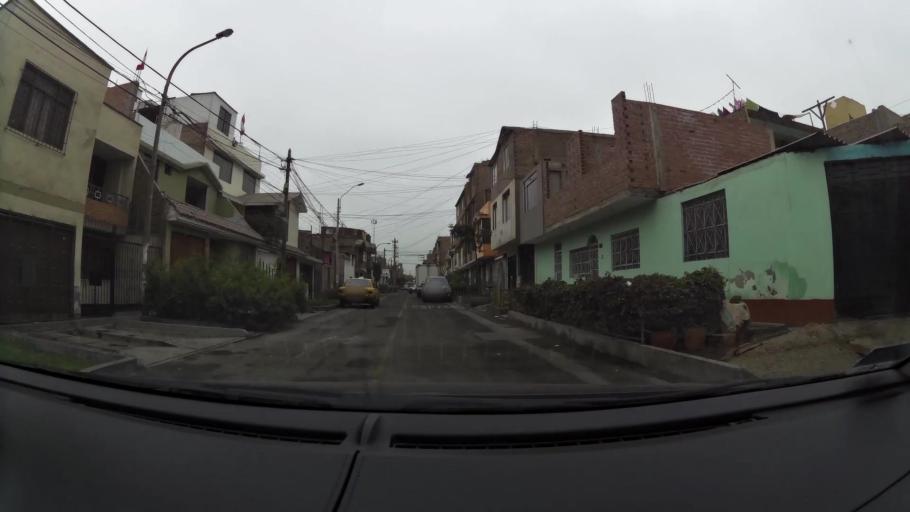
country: PE
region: Lima
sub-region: Lima
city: Independencia
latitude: -11.9749
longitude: -77.0751
